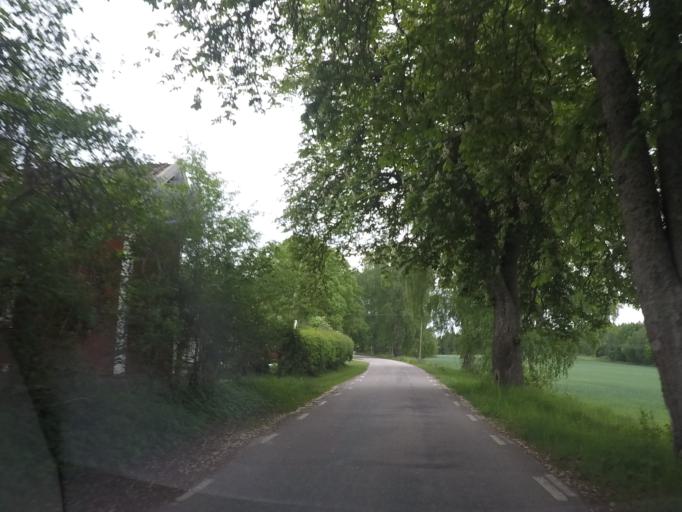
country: SE
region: Soedermanland
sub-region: Nykopings Kommun
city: Stigtomta
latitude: 58.8671
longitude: 16.8943
